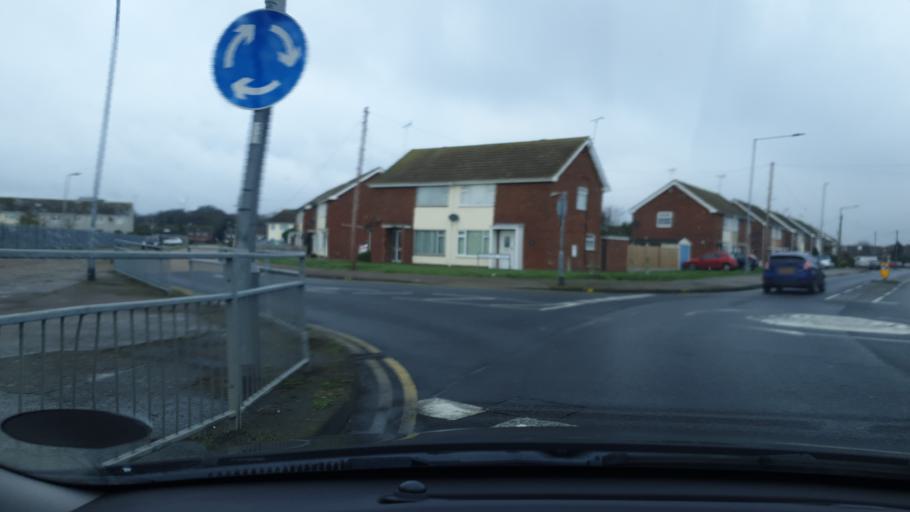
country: GB
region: England
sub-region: Essex
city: Clacton-on-Sea
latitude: 51.7994
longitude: 1.1304
